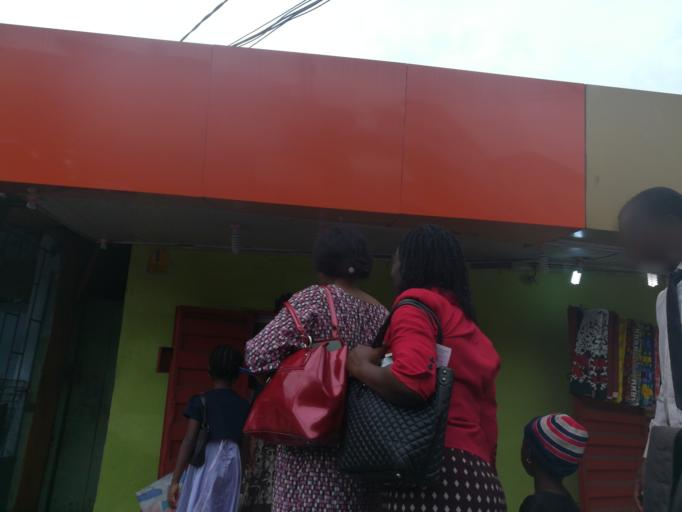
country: NG
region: Lagos
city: Ojota
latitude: 6.5727
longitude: 3.3713
